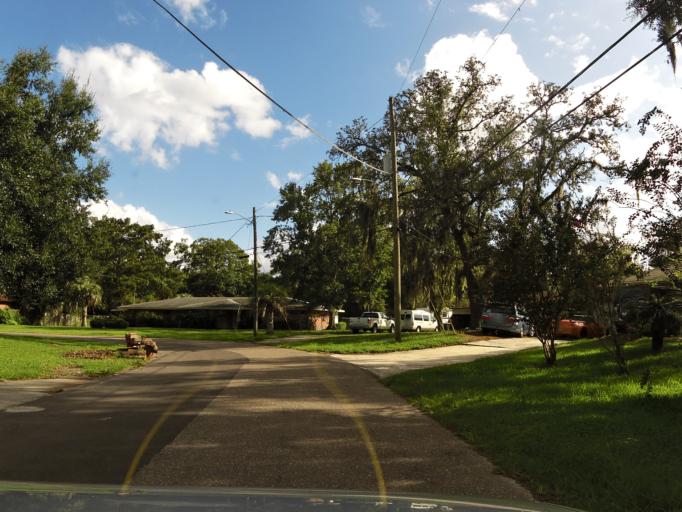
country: US
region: Florida
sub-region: Duval County
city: Jacksonville
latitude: 30.2894
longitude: -81.7396
